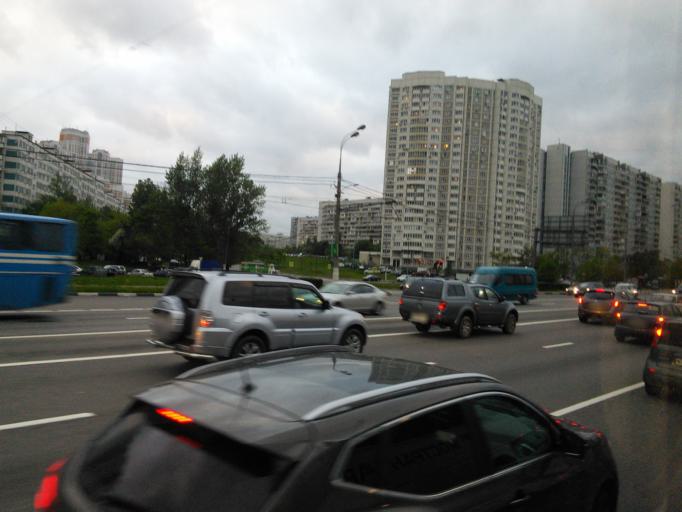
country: RU
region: Moscow
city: Biryulevo
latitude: 55.5802
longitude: 37.6836
